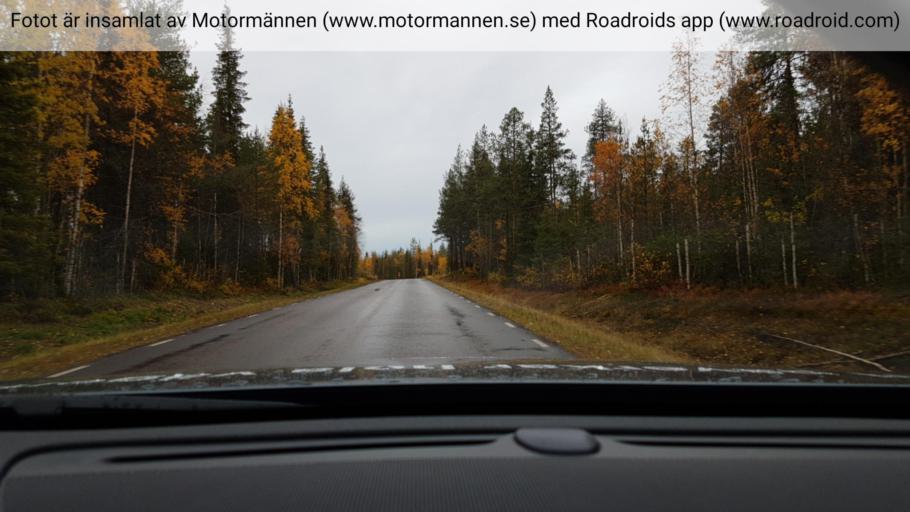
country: SE
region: Norrbotten
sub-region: Pajala Kommun
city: Pajala
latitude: 67.1636
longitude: 22.6569
